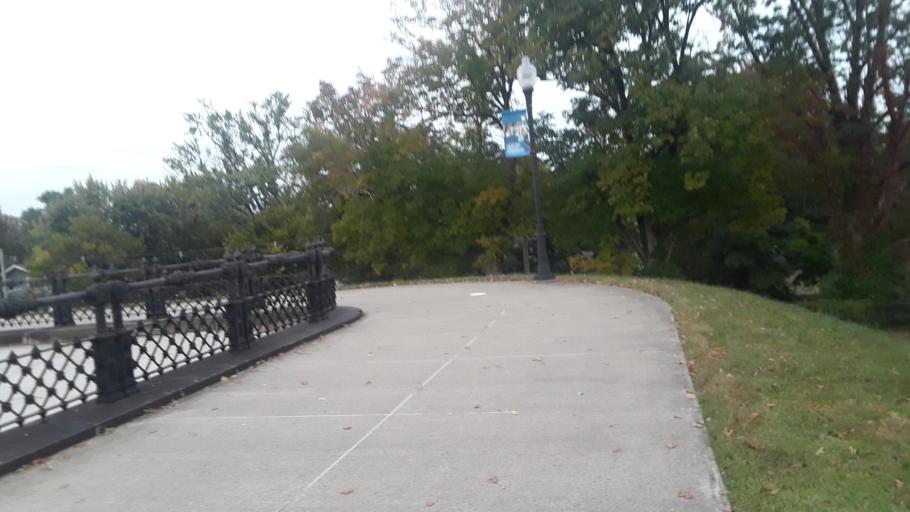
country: US
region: Kentucky
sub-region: Jefferson County
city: Saint Matthews
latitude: 38.2549
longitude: -85.6784
